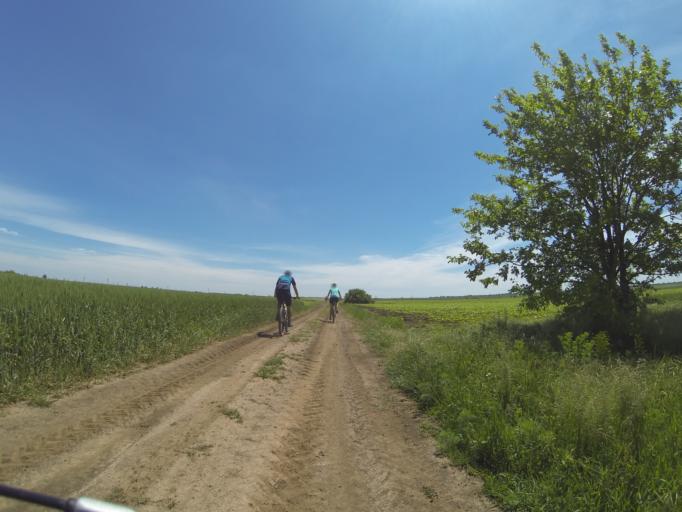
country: RO
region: Dolj
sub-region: Comuna Leu
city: Zanoaga
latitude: 44.1769
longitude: 24.0872
